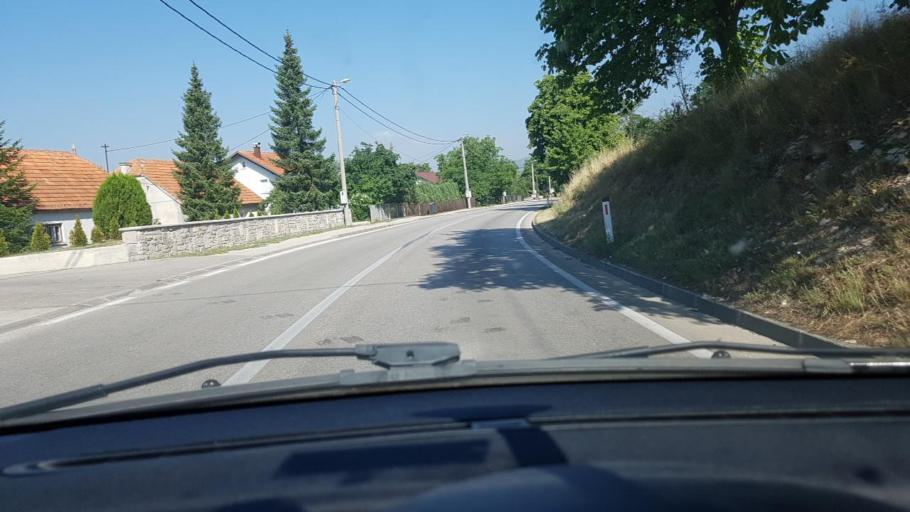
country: BA
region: Federation of Bosnia and Herzegovina
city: Livno
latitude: 43.8333
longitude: 16.9861
